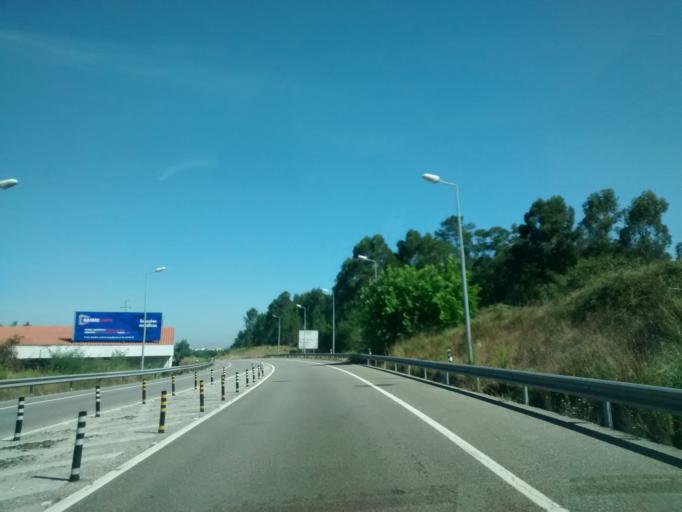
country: PT
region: Aveiro
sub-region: Anadia
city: Sangalhos
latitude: 40.4848
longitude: -8.4812
